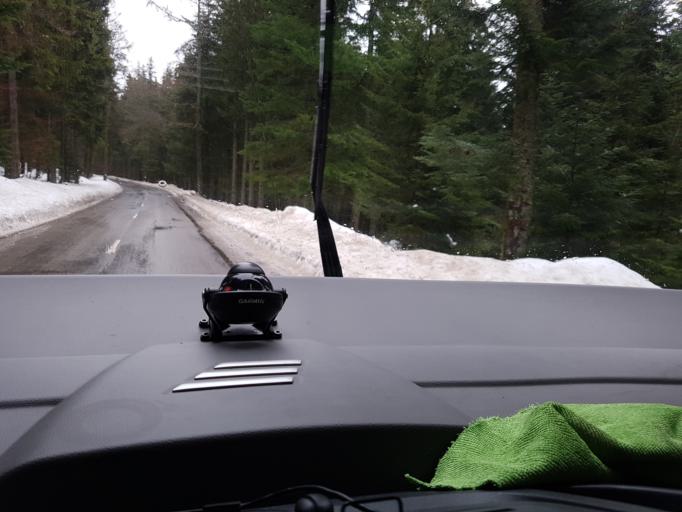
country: FR
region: Lorraine
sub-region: Departement des Vosges
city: Plainfaing
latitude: 48.1600
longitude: 7.0764
